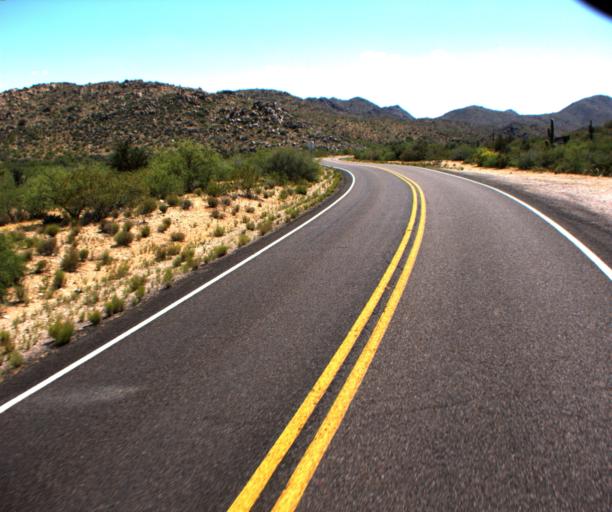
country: US
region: Arizona
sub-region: Yavapai County
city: Bagdad
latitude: 34.4879
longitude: -113.1826
